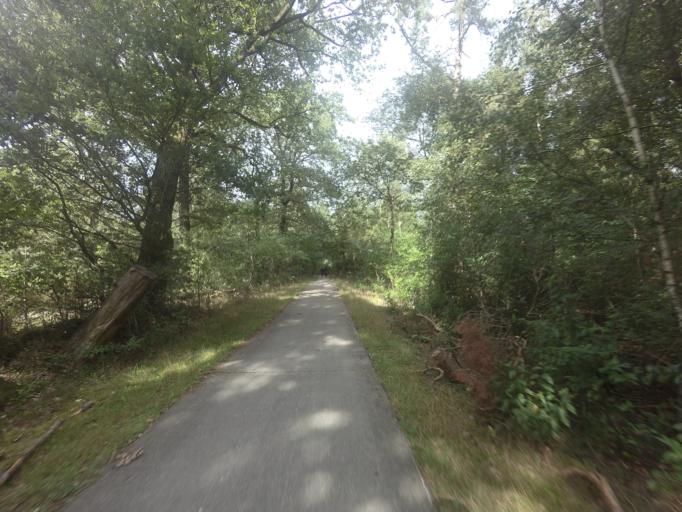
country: NL
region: Drenthe
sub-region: Gemeente Westerveld
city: Dwingeloo
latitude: 52.8775
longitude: 6.2835
